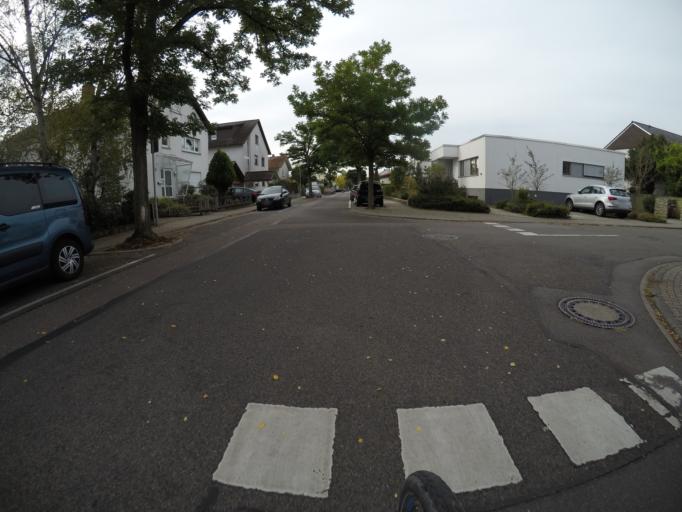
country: DE
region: Baden-Wuerttemberg
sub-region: Karlsruhe Region
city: Walldorf
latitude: 49.3107
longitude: 8.6357
